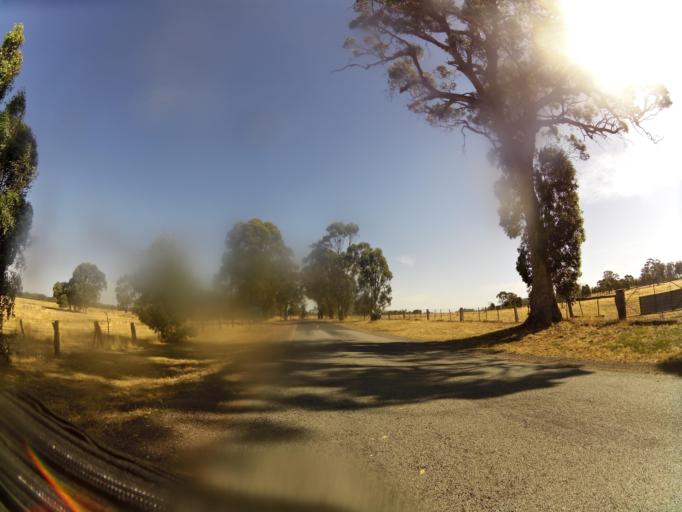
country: AU
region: Victoria
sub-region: Campaspe
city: Kyabram
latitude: -36.8948
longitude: 145.1068
